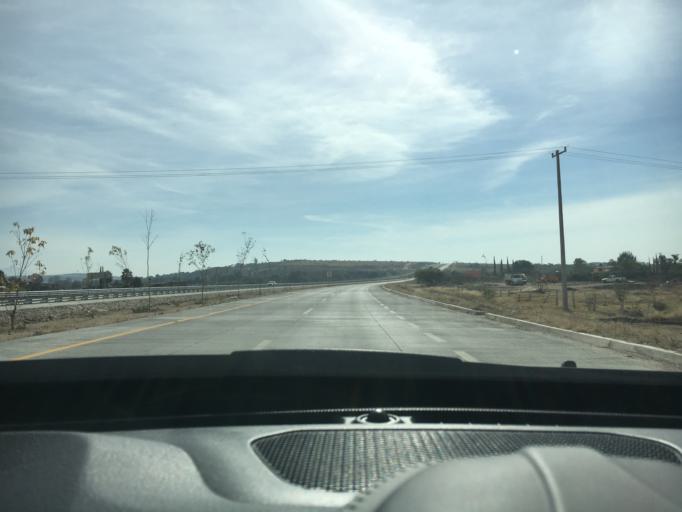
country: MX
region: Guanajuato
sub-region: Leon
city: Ladrilleras del Refugio
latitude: 21.0751
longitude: -101.5426
